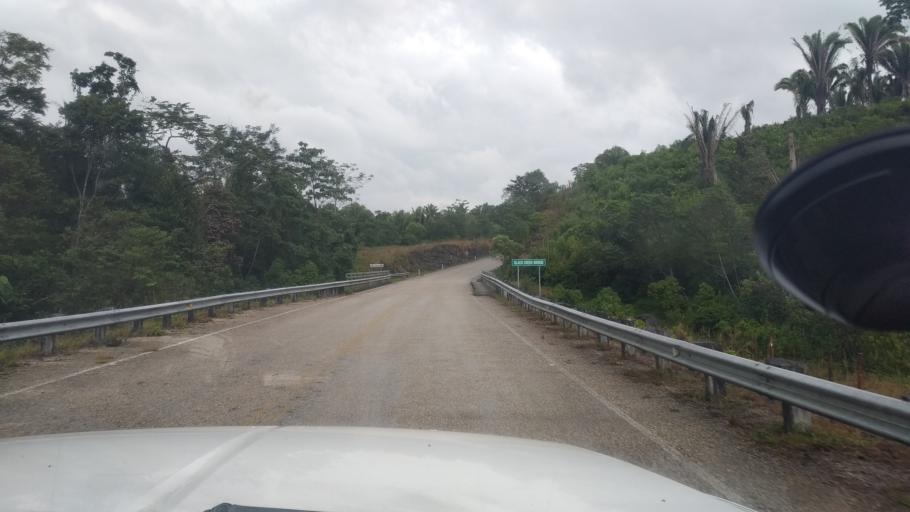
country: GT
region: Peten
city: San Luis
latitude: 16.1930
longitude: -89.1709
